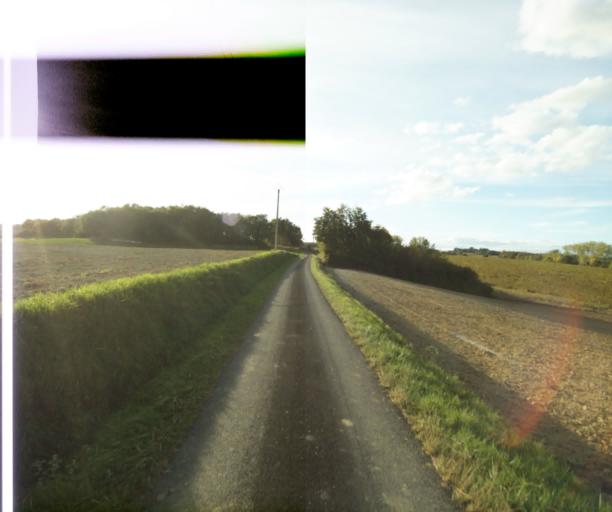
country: FR
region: Midi-Pyrenees
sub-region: Departement du Gers
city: Gondrin
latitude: 43.8897
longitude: 0.2617
